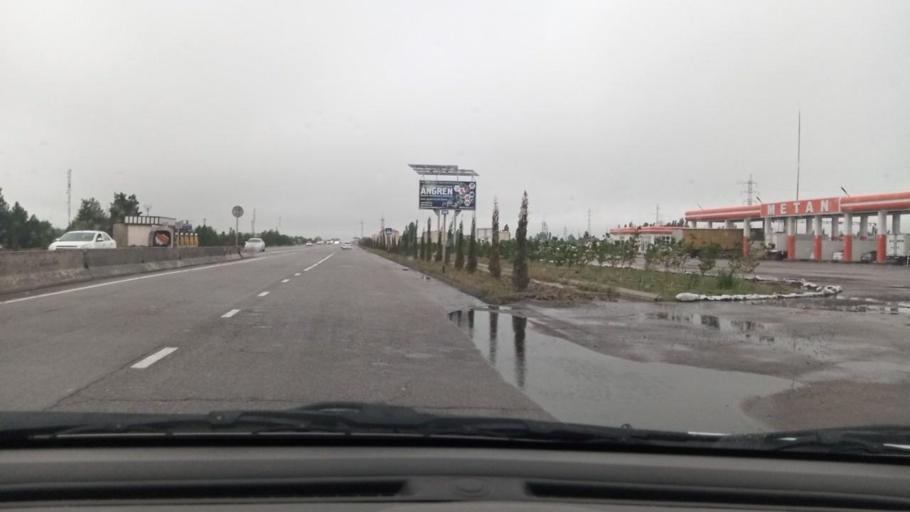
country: UZ
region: Toshkent
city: Angren
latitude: 41.0171
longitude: 70.1131
